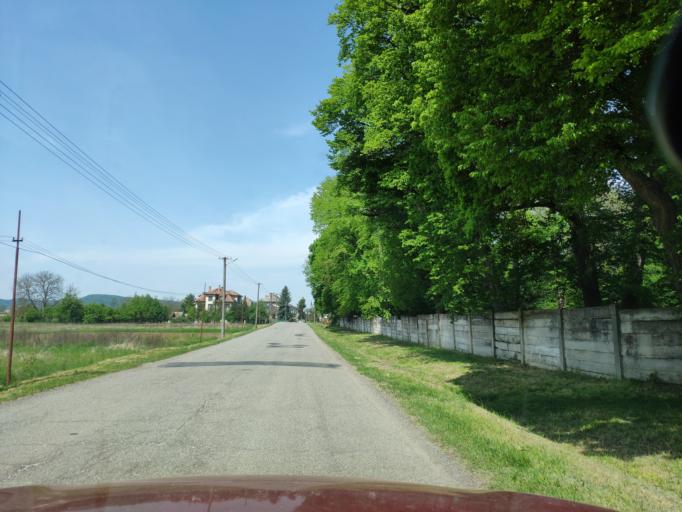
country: SK
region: Banskobystricky
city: Rimavska Sobota
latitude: 48.4493
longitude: 20.1117
